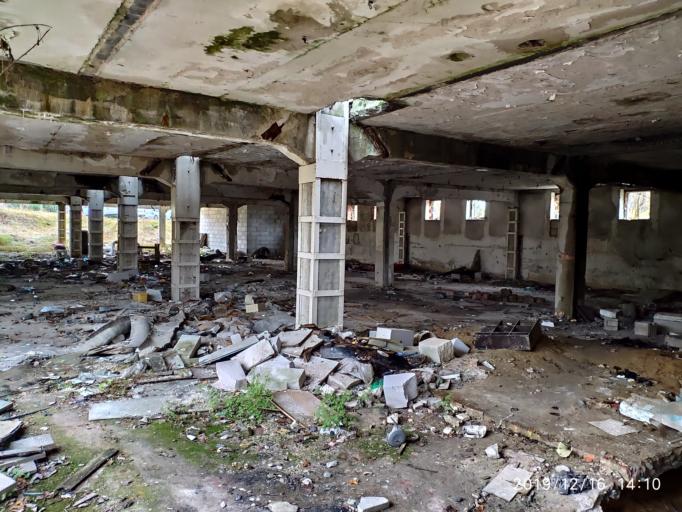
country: PL
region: Lubusz
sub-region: Zielona Gora
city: Zielona Gora
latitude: 51.9473
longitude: 15.4908
